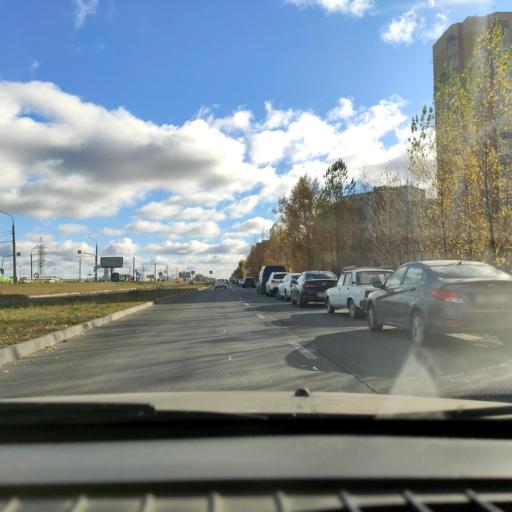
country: RU
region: Samara
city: Tol'yatti
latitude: 53.5489
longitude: 49.3342
